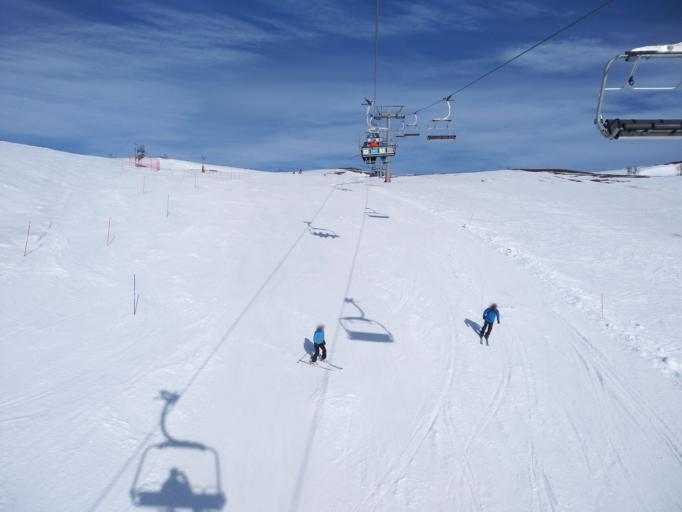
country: NO
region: Aust-Agder
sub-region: Bykle
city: Hovden
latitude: 59.5766
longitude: 7.3174
